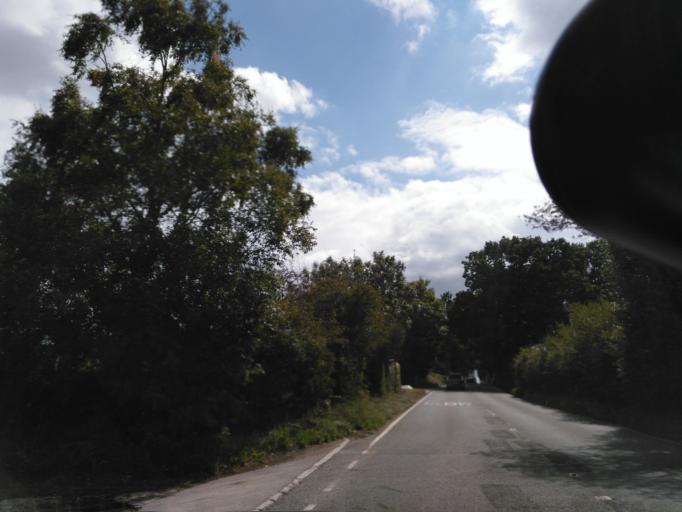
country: GB
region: England
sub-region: Dorset
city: Lytchett Matravers
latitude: 50.7650
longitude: -2.0602
